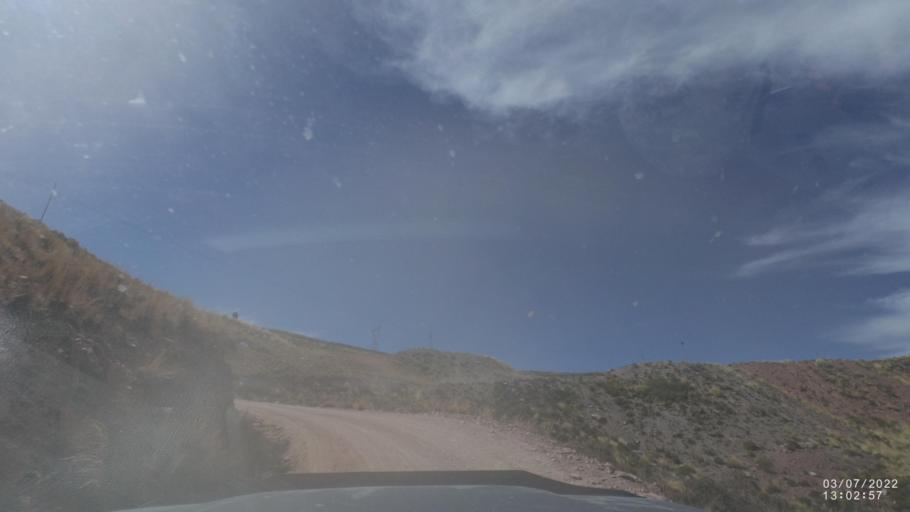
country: BO
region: Cochabamba
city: Colchani
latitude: -17.7065
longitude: -66.6890
